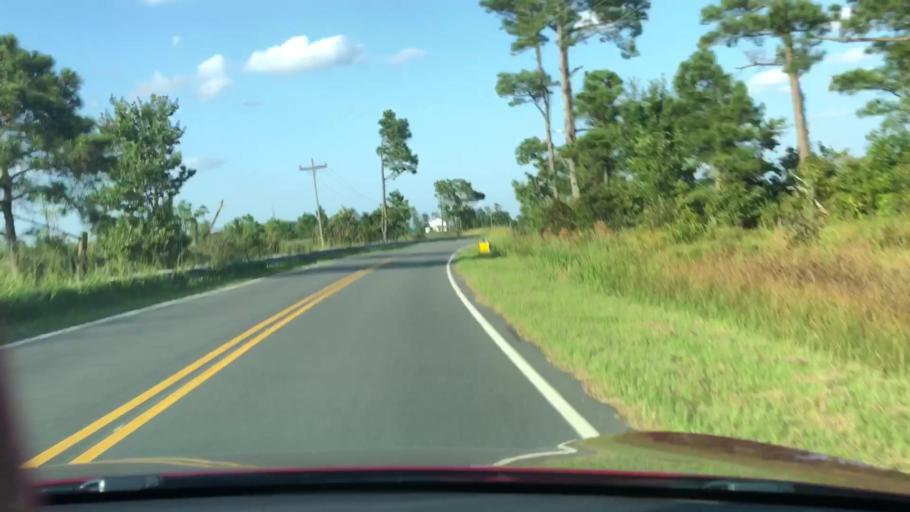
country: US
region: North Carolina
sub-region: Dare County
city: Wanchese
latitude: 35.6929
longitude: -75.7796
